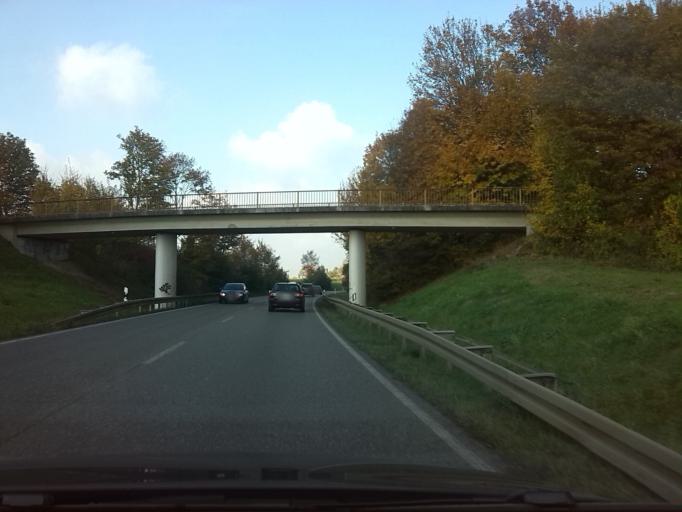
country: DE
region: Baden-Wuerttemberg
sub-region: Regierungsbezirk Stuttgart
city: Stuttgart Muehlhausen
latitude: 48.8290
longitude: 9.2511
